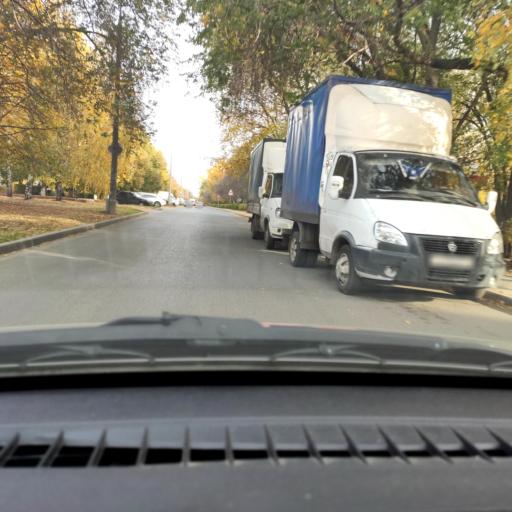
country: RU
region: Samara
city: Tol'yatti
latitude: 53.5258
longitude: 49.2979
